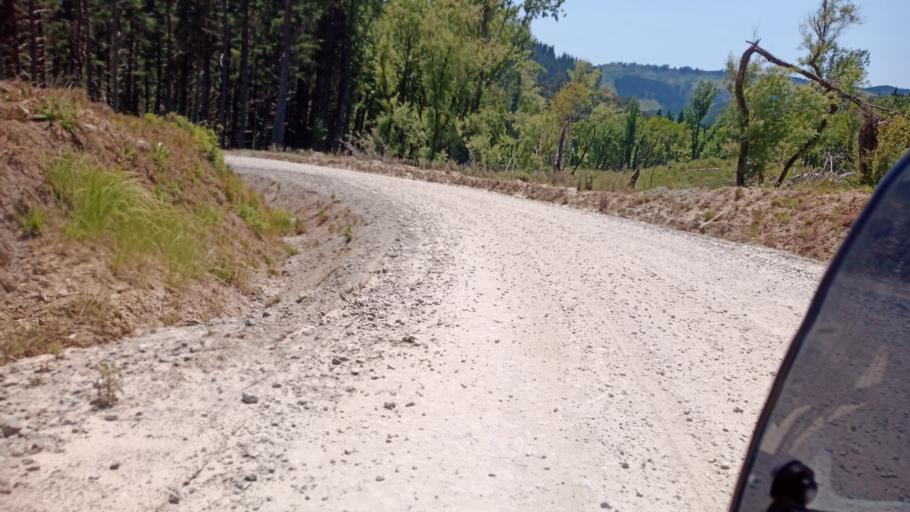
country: NZ
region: Gisborne
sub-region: Gisborne District
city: Gisborne
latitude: -38.2846
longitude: 178.0067
